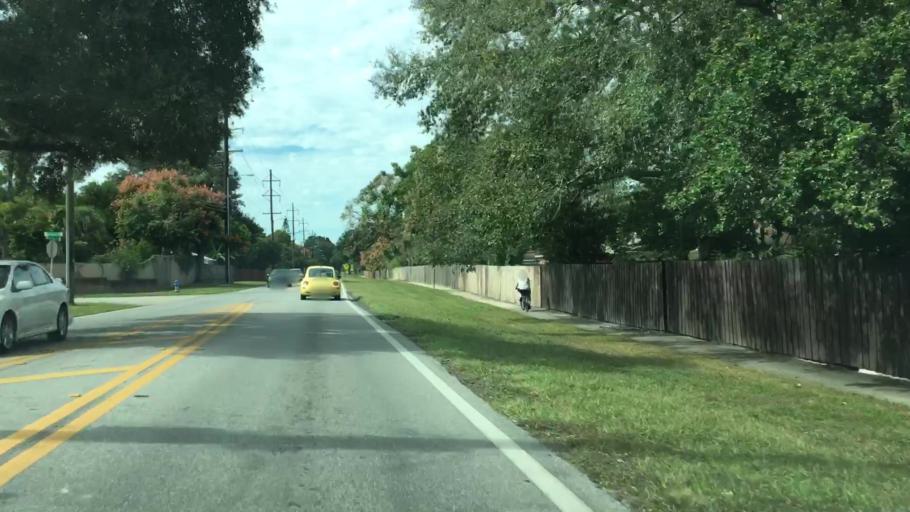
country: US
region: Florida
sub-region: Orange County
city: Conway
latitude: 28.5062
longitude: -81.3239
